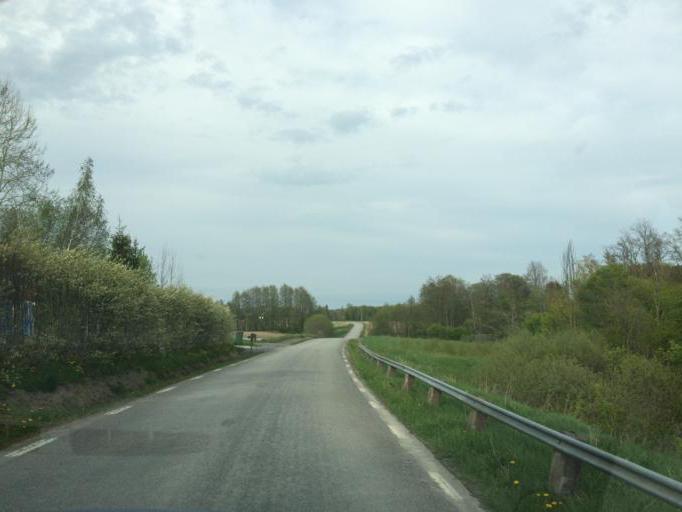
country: SE
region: Vaestmanland
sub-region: Kopings Kommun
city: Koping
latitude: 59.5881
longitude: 15.9872
